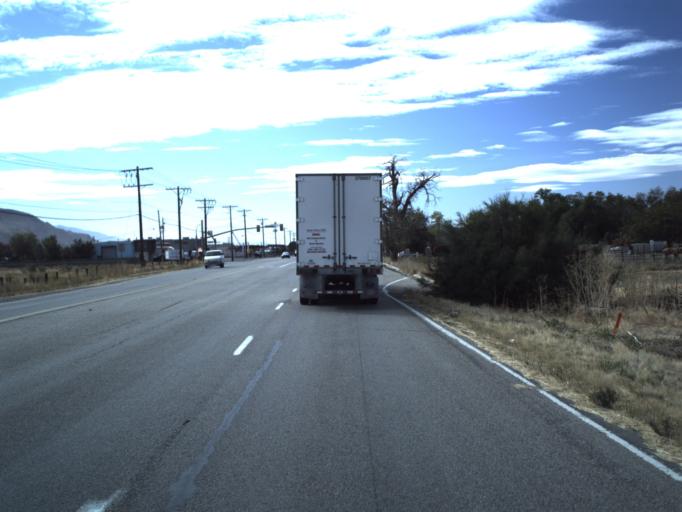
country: US
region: Utah
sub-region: Davis County
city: North Salt Lake
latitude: 40.8634
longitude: -111.9300
